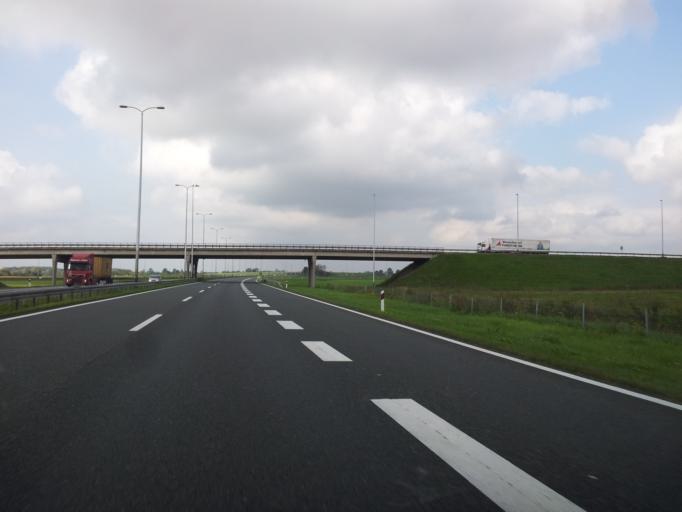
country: HR
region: Brodsko-Posavska
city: Okucani
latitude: 45.2279
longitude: 17.2201
